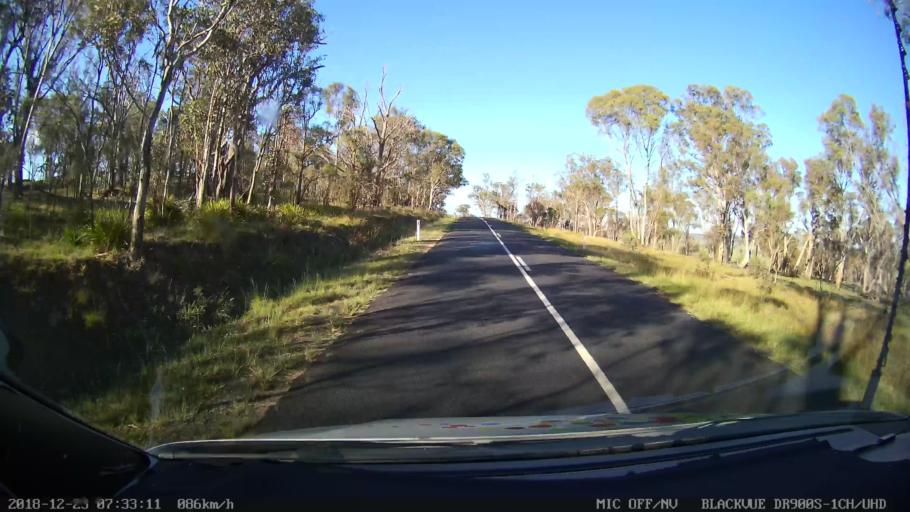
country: AU
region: New South Wales
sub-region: Armidale Dumaresq
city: Enmore
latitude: -30.5101
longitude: 152.1072
